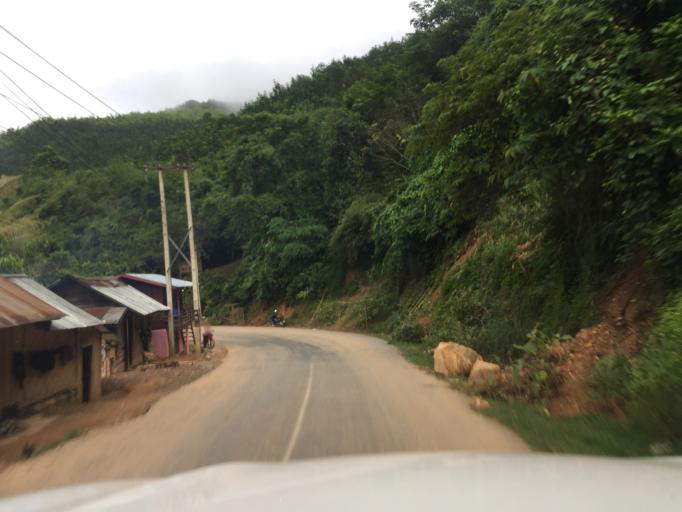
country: LA
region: Phongsali
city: Khoa
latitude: 21.1038
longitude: 102.2868
